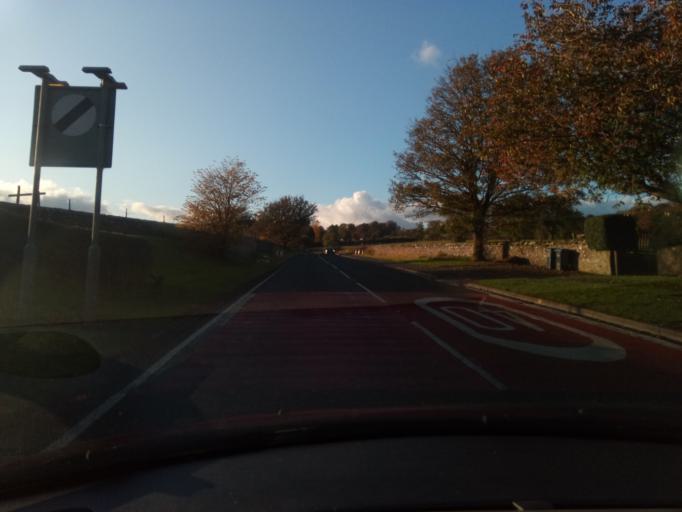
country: GB
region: England
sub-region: County Durham
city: Stanhope
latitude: 54.7490
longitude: -2.0209
